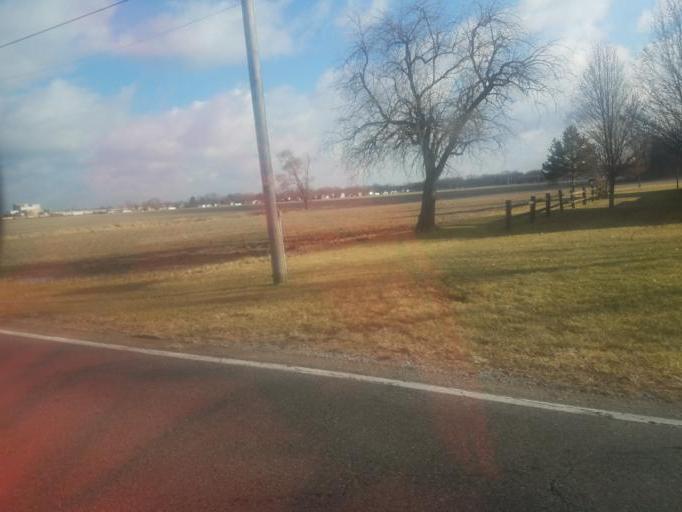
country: US
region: Ohio
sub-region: Marion County
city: Marion
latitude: 40.5787
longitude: -83.1645
